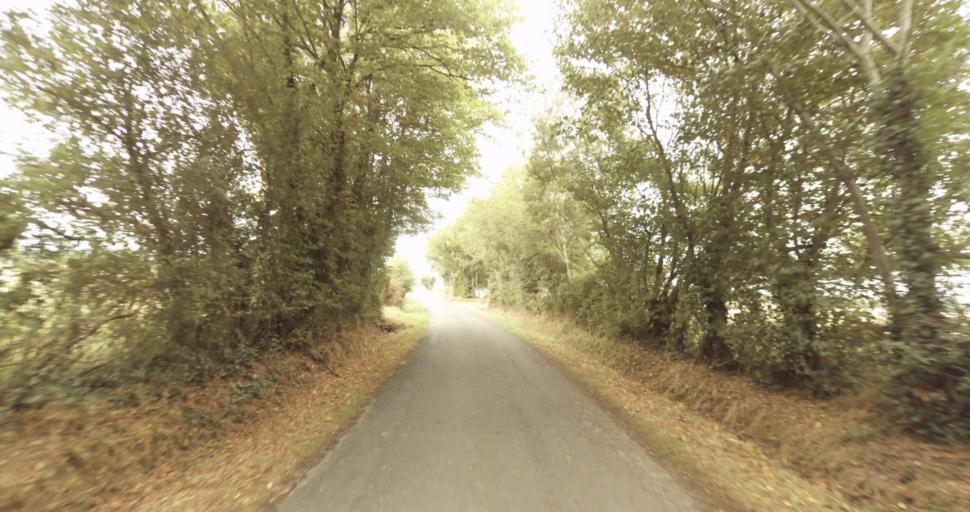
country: FR
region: Lower Normandy
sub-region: Departement de l'Orne
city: Sainte-Gauburge-Sainte-Colombe
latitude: 48.7206
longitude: 0.4882
